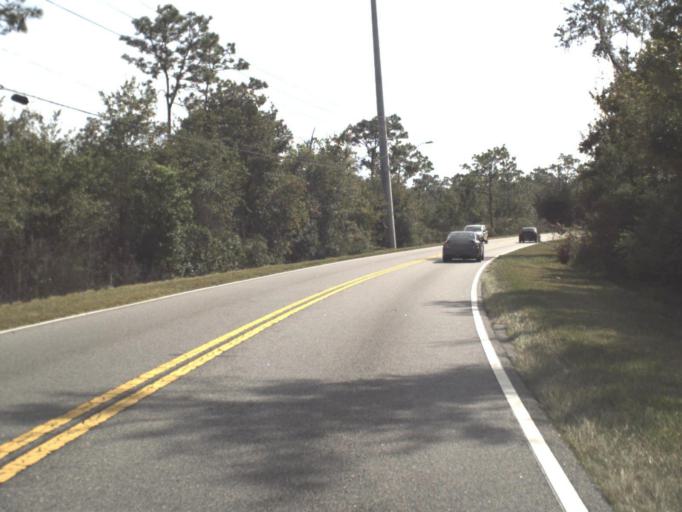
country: US
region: Florida
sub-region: Osceola County
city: Poinciana
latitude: 28.1961
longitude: -81.4701
